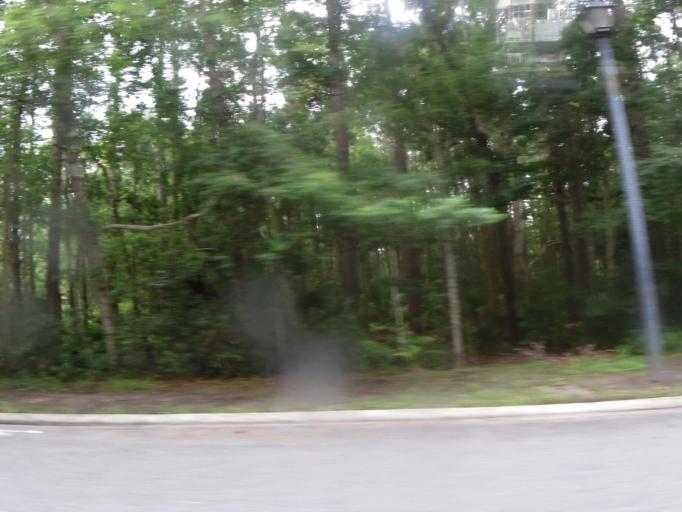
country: US
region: Florida
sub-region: Saint Johns County
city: Ponte Vedra Beach
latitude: 30.2548
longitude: -81.4545
